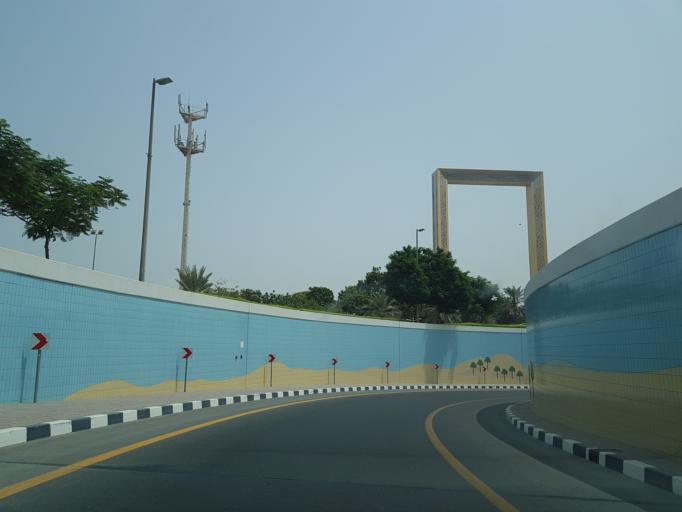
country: AE
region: Ash Shariqah
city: Sharjah
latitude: 25.2324
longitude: 55.2968
